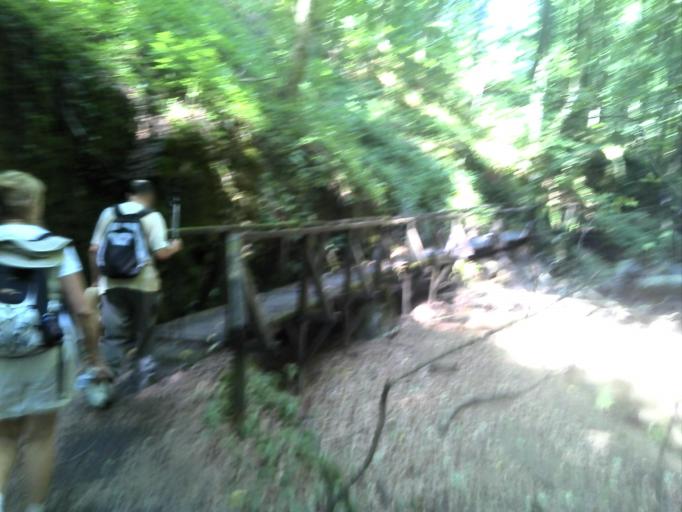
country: HU
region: Baranya
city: Pecs
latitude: 46.1466
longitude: 18.2120
